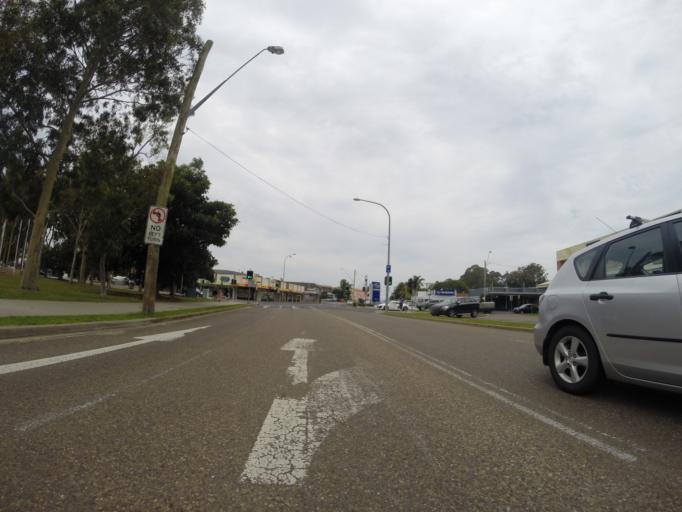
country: AU
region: New South Wales
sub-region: Eurobodalla
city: Batemans Bay
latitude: -35.7085
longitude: 150.1769
